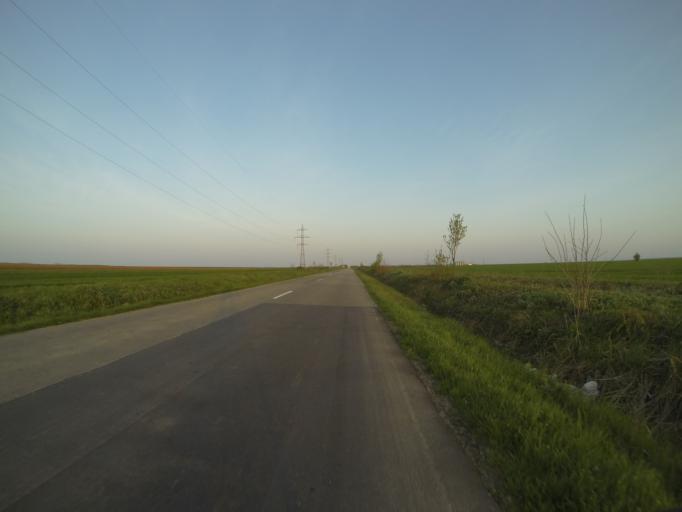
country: RO
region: Dolj
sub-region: Comuna Dranicu
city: Dranic
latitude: 44.0628
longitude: 23.8180
